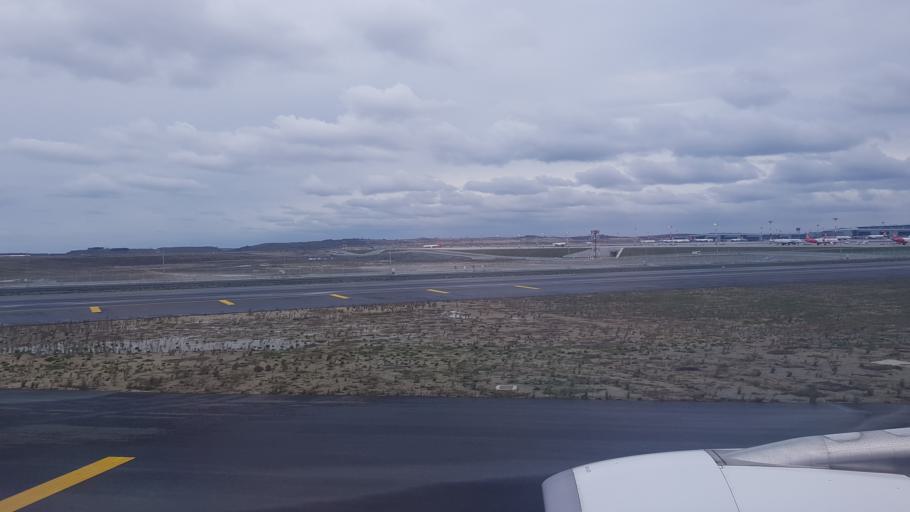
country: TR
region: Istanbul
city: Durusu
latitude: 41.2805
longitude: 28.7282
